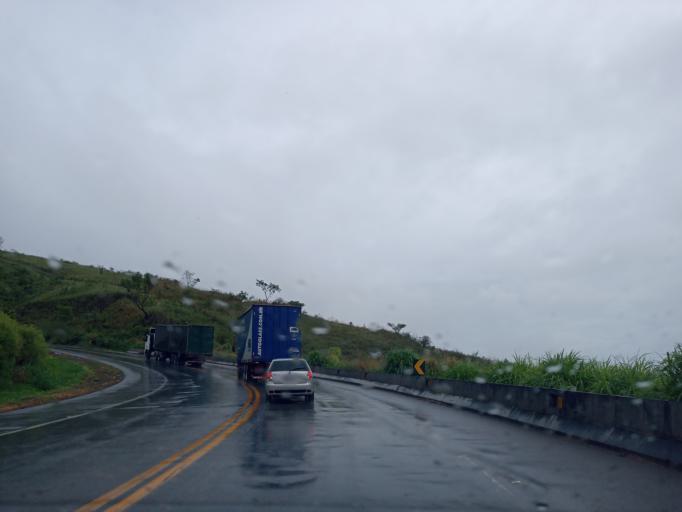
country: BR
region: Minas Gerais
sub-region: Luz
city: Luz
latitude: -19.7196
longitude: -45.8775
